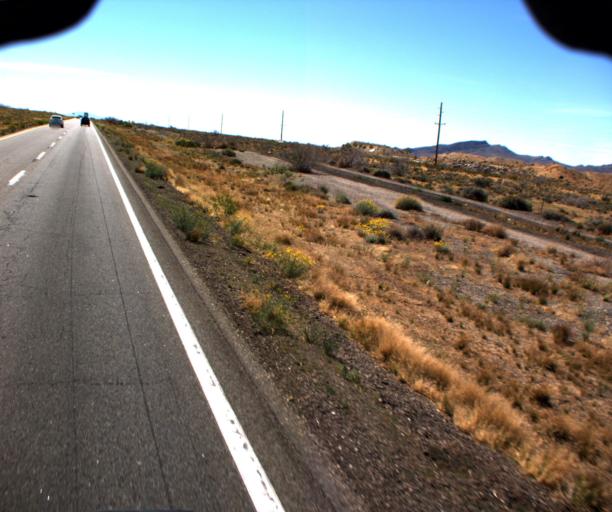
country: US
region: Arizona
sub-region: Mohave County
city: Dolan Springs
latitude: 35.4247
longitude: -114.2797
